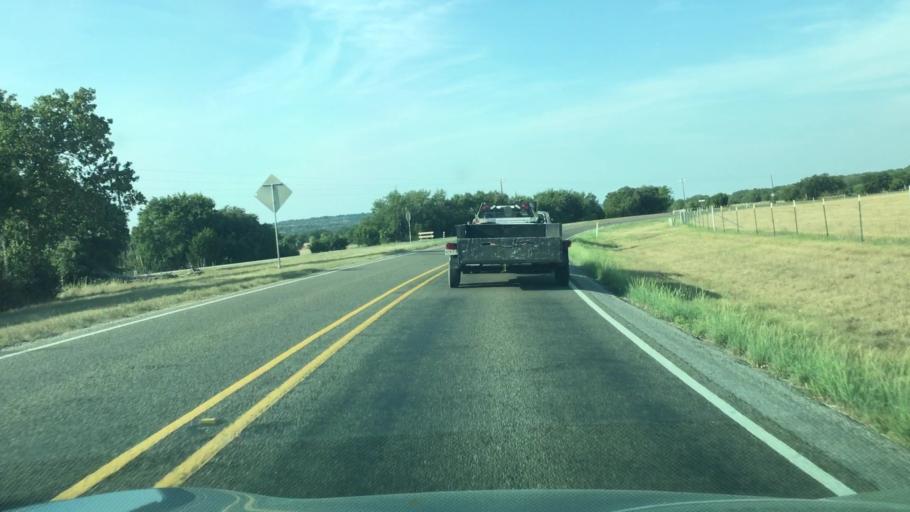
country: US
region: Texas
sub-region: Hays County
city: Dripping Springs
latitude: 30.1892
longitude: -98.2151
